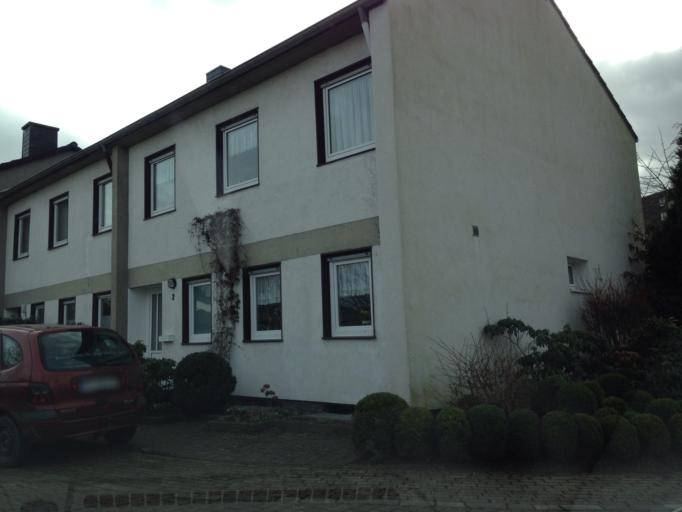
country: DE
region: North Rhine-Westphalia
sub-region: Regierungsbezirk Munster
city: Muenster
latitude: 51.9997
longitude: 7.5972
